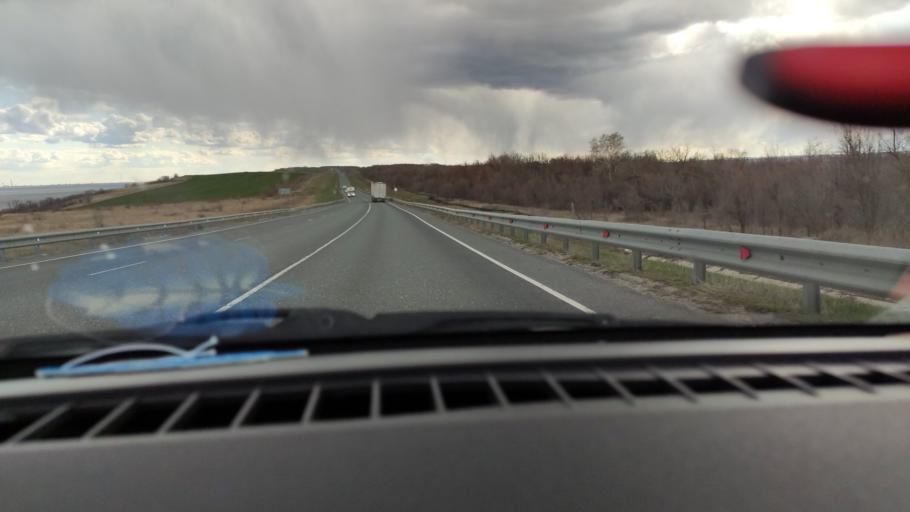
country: RU
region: Saratov
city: Balakovo
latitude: 52.1964
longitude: 47.8591
